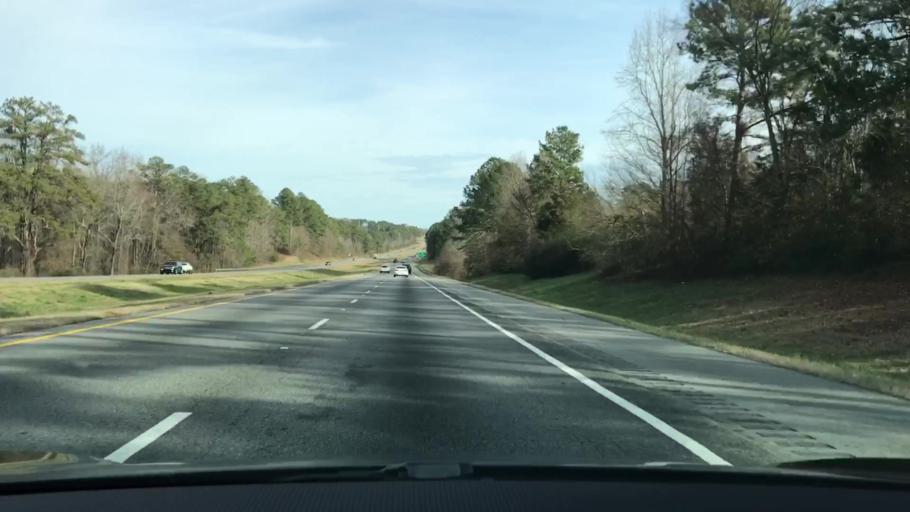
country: US
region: Georgia
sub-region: Walton County
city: Social Circle
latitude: 33.6113
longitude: -83.7188
